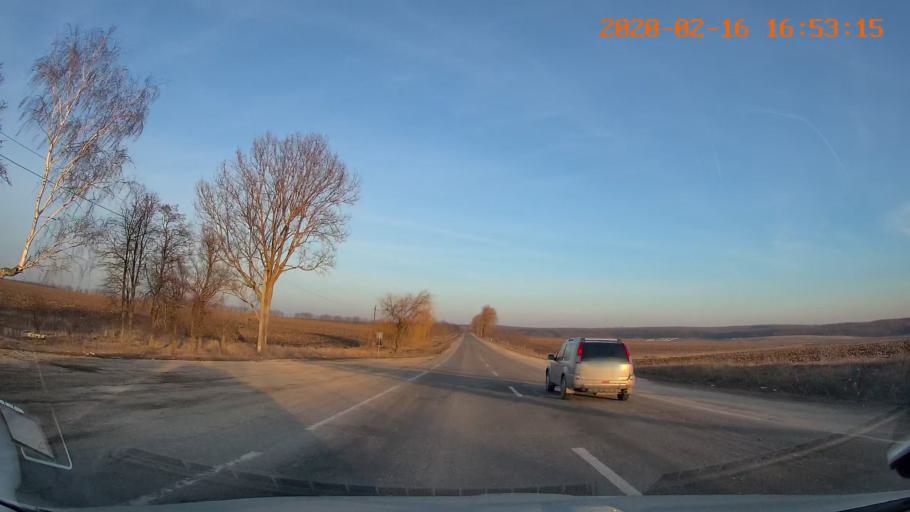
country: MD
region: Briceni
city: Briceni
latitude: 48.3166
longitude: 26.9785
